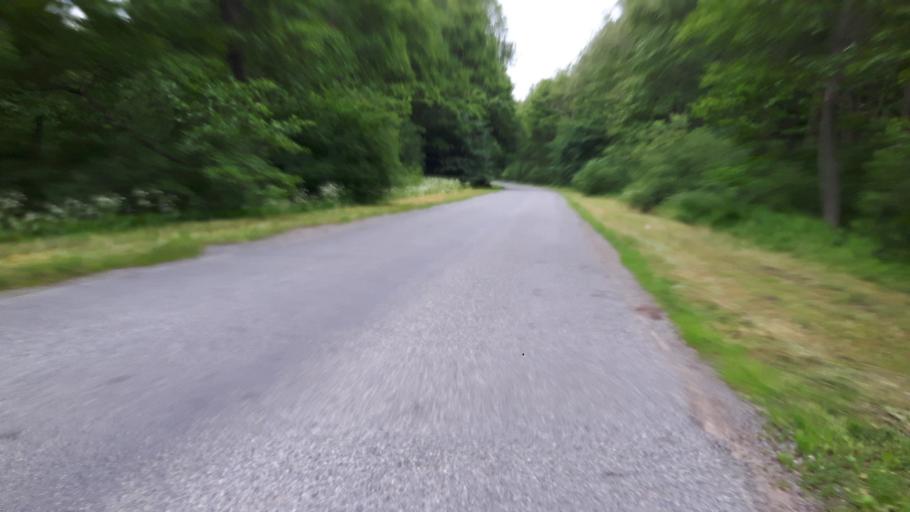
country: LV
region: Liepaja
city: Vec-Liepaja
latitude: 56.5737
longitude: 21.0233
